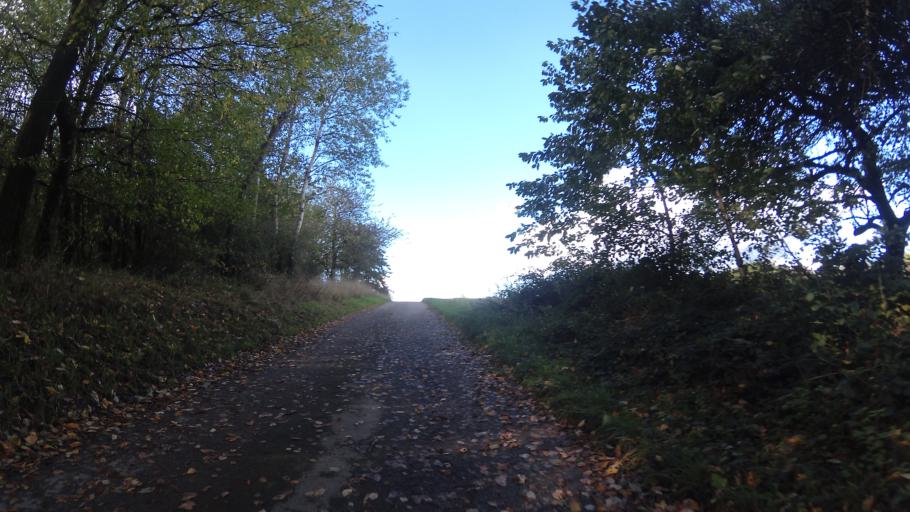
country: DE
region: Saarland
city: Marpingen
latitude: 49.4515
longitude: 7.0329
